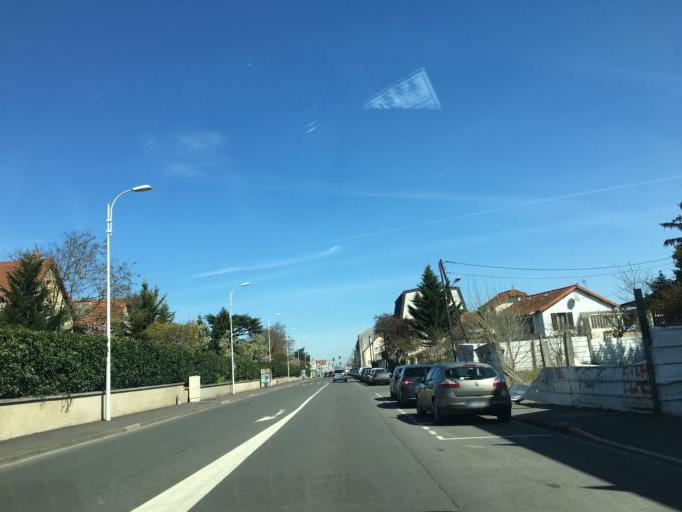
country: FR
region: Ile-de-France
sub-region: Departement de l'Essonne
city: Draveil
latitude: 48.6882
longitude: 2.4097
